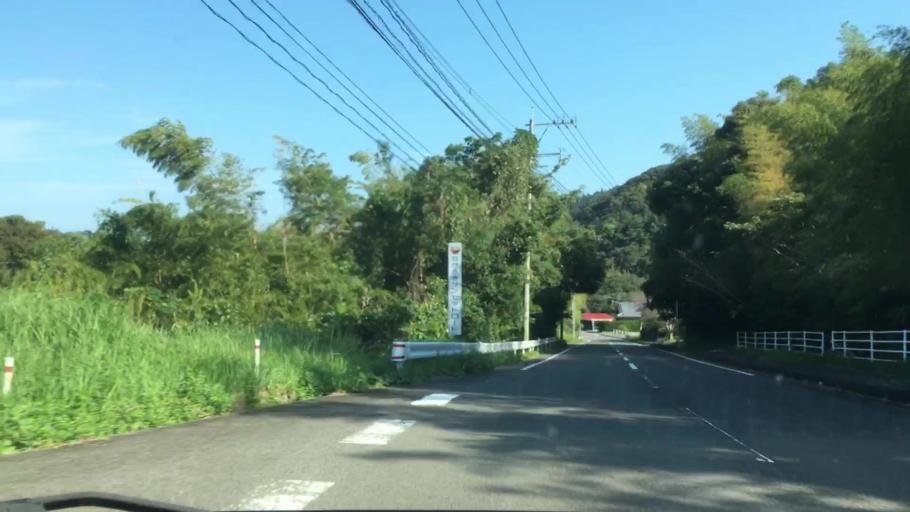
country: JP
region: Nagasaki
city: Sasebo
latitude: 33.0062
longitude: 129.6566
